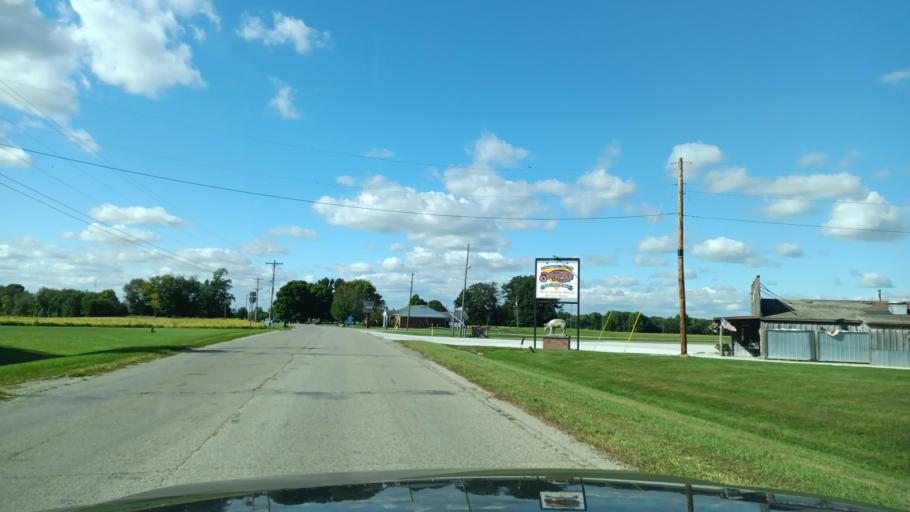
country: US
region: Indiana
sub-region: Fountain County
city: Covington
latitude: 40.1249
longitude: -87.3822
